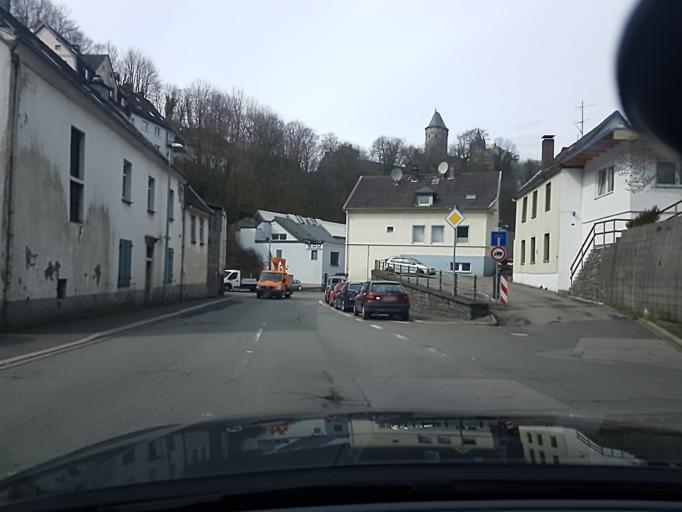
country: DE
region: North Rhine-Westphalia
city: Altena
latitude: 51.2975
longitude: 7.6779
